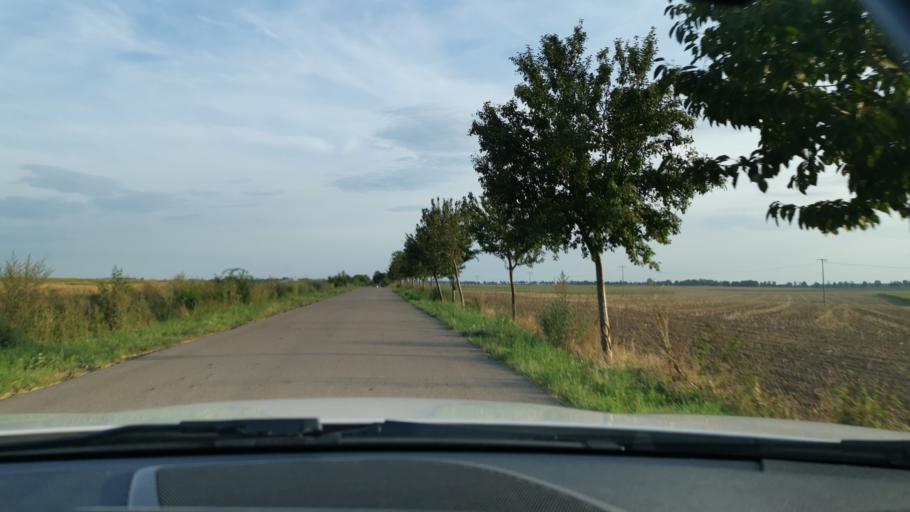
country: DE
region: Brandenburg
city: Juterbog
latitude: 51.9492
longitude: 13.1389
